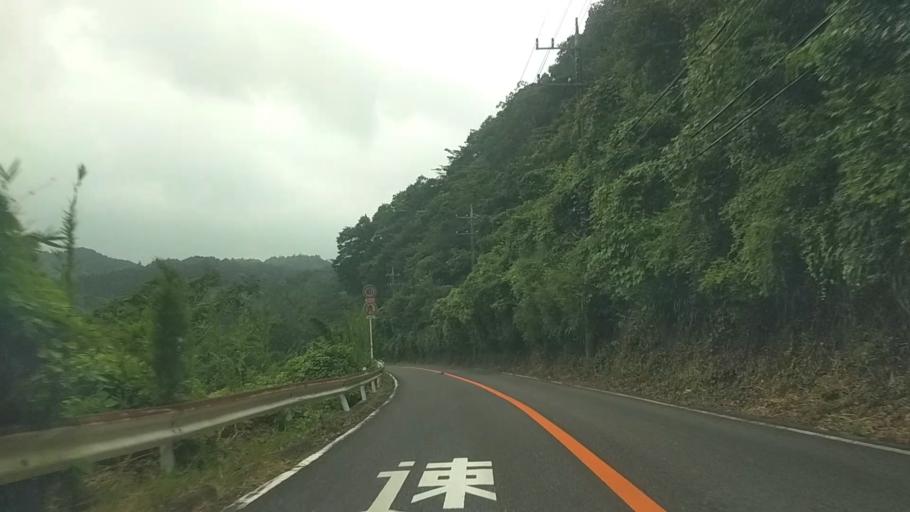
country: JP
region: Chiba
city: Kawaguchi
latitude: 35.2125
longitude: 140.0702
